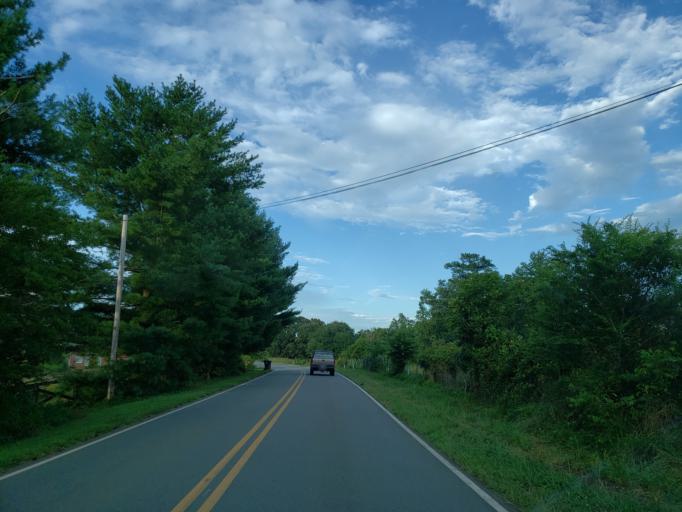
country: US
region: Georgia
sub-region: Cherokee County
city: Ball Ground
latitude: 34.3300
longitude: -84.4585
